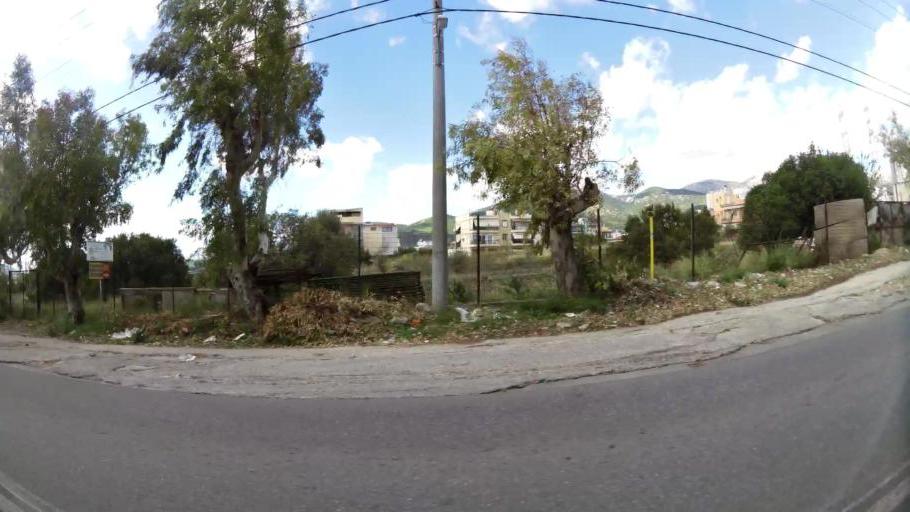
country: GR
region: Attica
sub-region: Nomarchia Anatolikis Attikis
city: Acharnes
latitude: 38.1037
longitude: 23.7427
